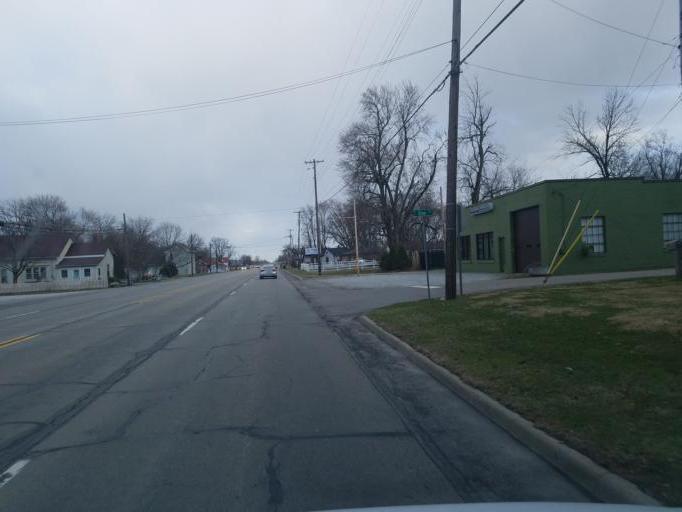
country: US
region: Indiana
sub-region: Hancock County
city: New Palestine
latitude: 39.7816
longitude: -85.8446
